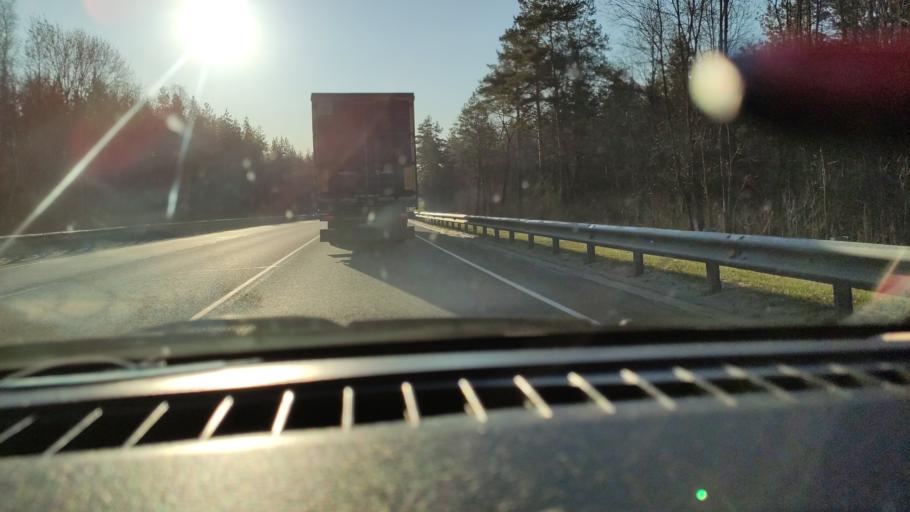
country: RU
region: Saratov
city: Vol'sk
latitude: 52.1062
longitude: 47.4301
